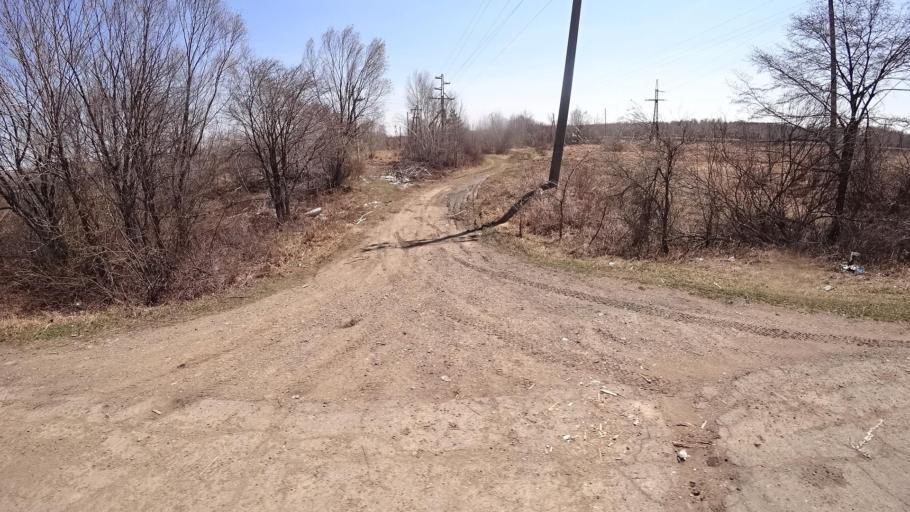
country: RU
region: Khabarovsk Krai
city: Khurba
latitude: 50.4035
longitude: 136.8693
